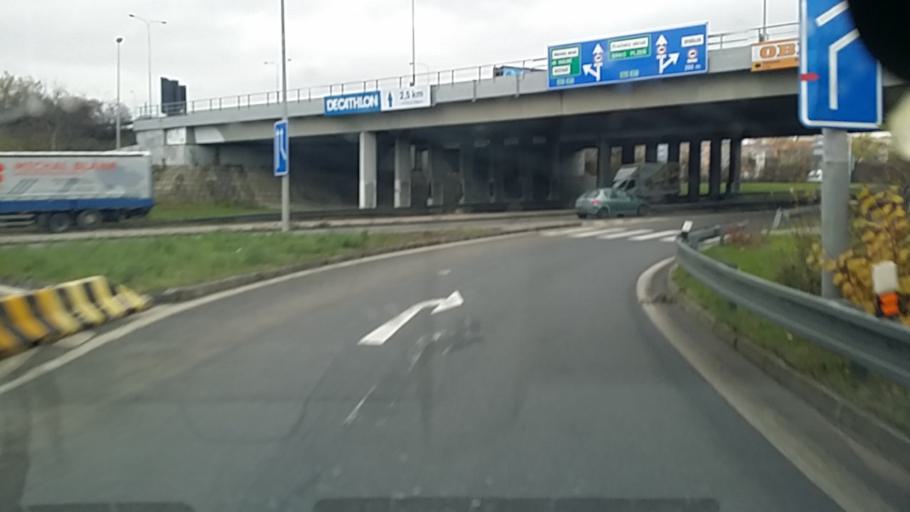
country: CZ
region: Praha
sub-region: Praha 8
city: Karlin
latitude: 50.0508
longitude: 14.4775
